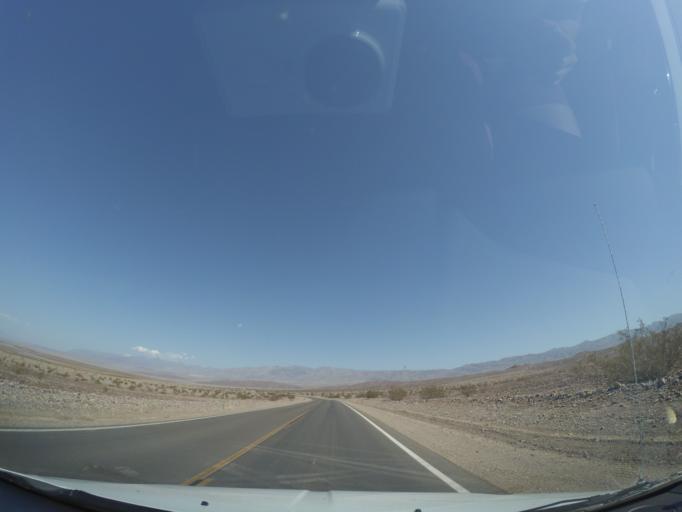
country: US
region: Nevada
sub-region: Nye County
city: Beatty
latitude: 36.5158
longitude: -116.8818
